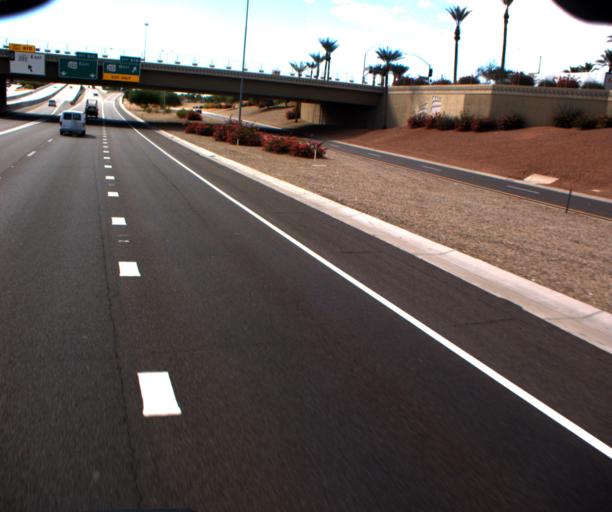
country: US
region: Arizona
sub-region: Maricopa County
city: Chandler
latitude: 33.2995
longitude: -111.8944
